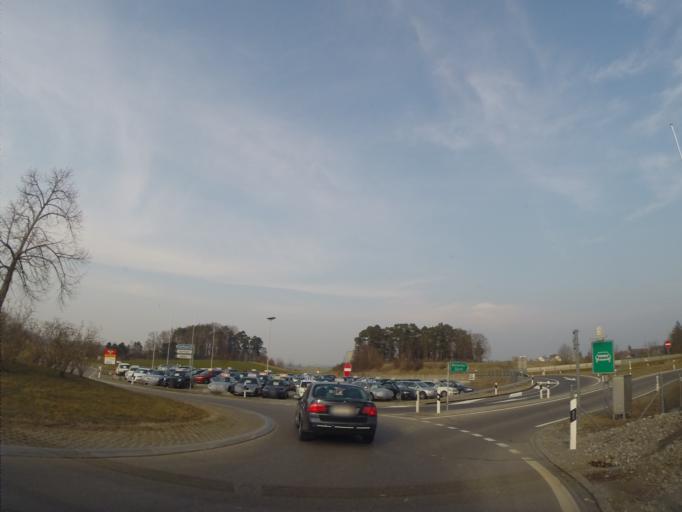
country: CH
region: Zurich
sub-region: Bezirk Andelfingen
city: Grossandelfingen
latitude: 47.5820
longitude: 8.6822
